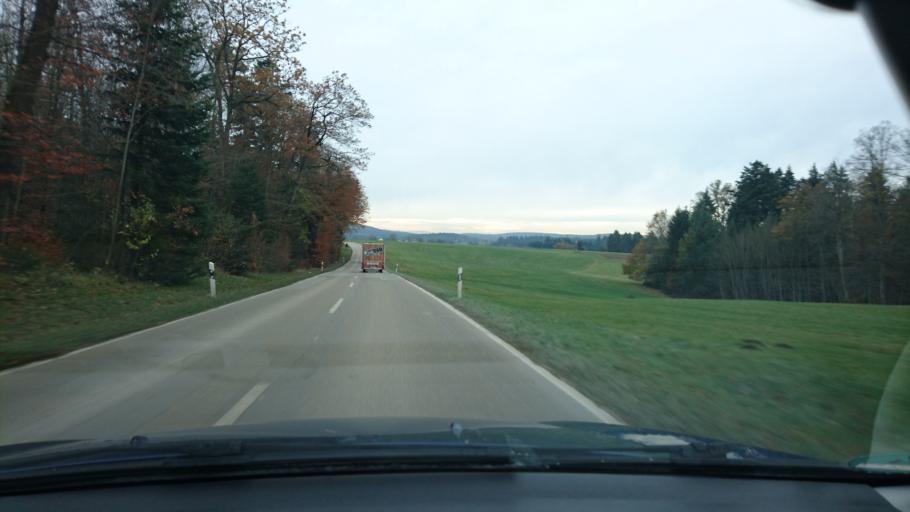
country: DE
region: Baden-Wuerttemberg
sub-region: Regierungsbezirk Stuttgart
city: Gschwend
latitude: 48.9244
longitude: 9.7060
